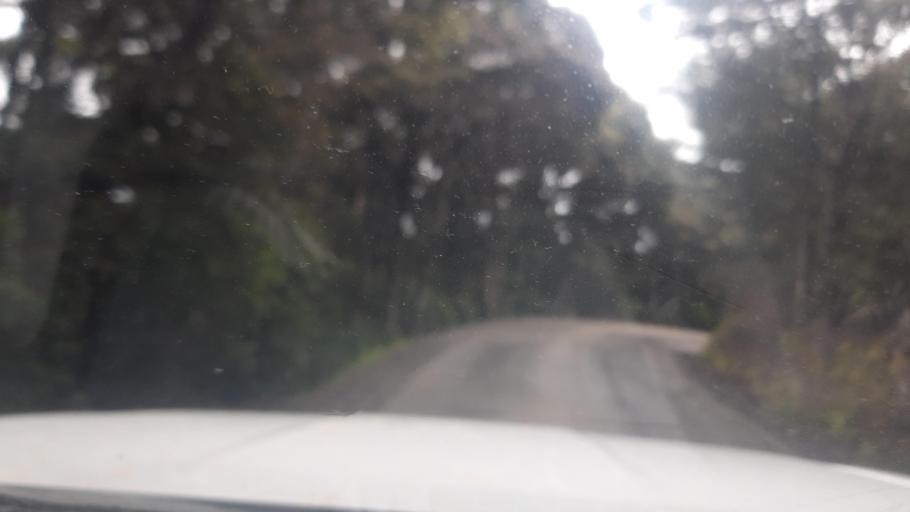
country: NZ
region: Northland
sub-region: Far North District
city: Taipa
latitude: -35.0663
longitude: 173.5273
